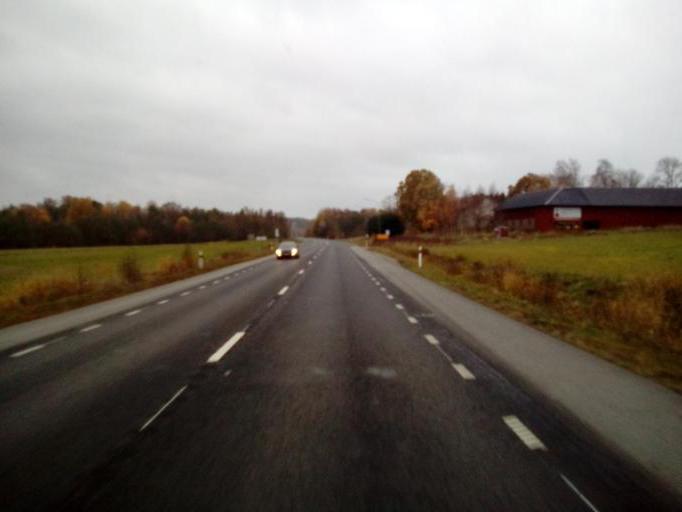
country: SE
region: OErebro
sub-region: Degerfors Kommun
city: Degerfors
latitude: 59.2647
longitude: 14.4405
